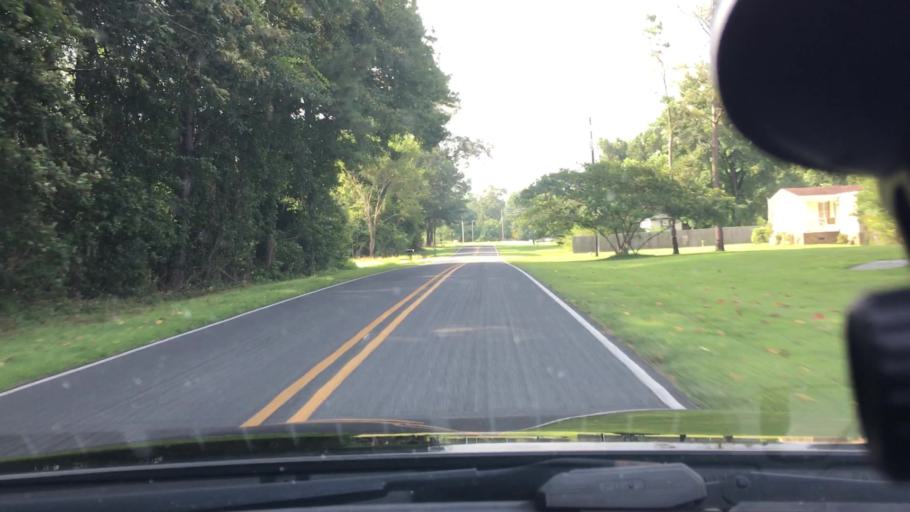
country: US
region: North Carolina
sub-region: Craven County
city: New Bern
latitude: 35.1818
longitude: -77.0570
